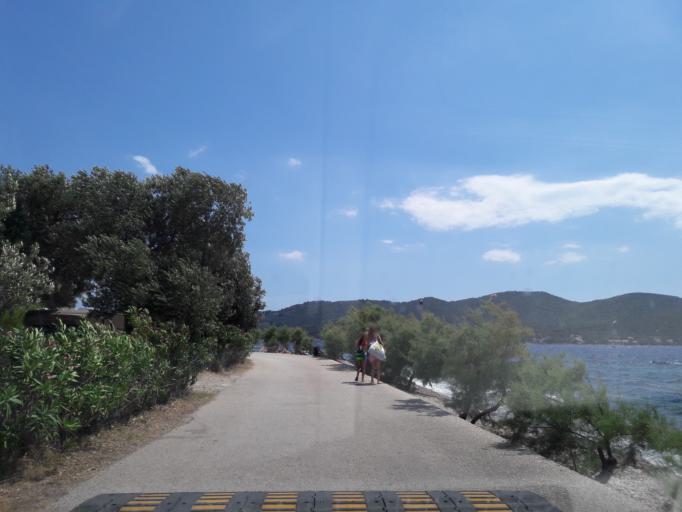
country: HR
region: Dubrovacko-Neretvanska
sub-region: Grad Korcula
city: Zrnovo
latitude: 42.9797
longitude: 17.1031
